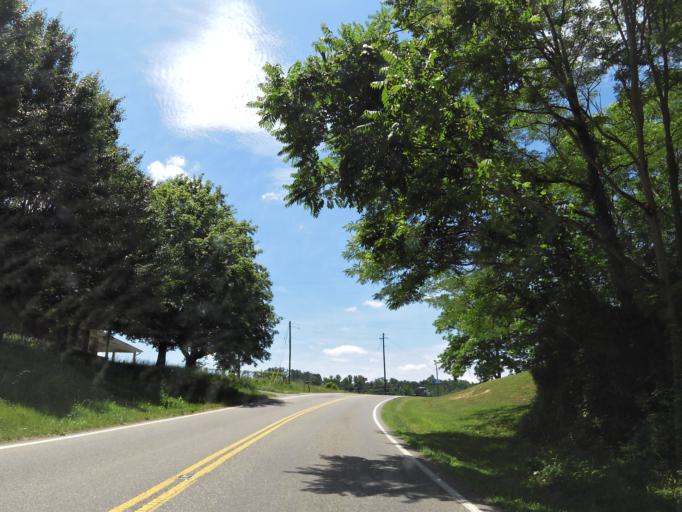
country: US
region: Tennessee
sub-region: Jefferson County
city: Dandridge
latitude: 35.9182
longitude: -83.3497
